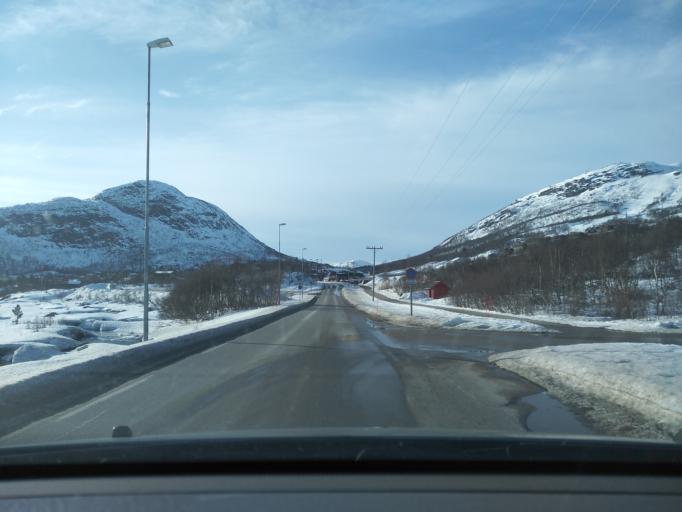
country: NO
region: Aust-Agder
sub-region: Bykle
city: Hovden
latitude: 59.5688
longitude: 7.3564
